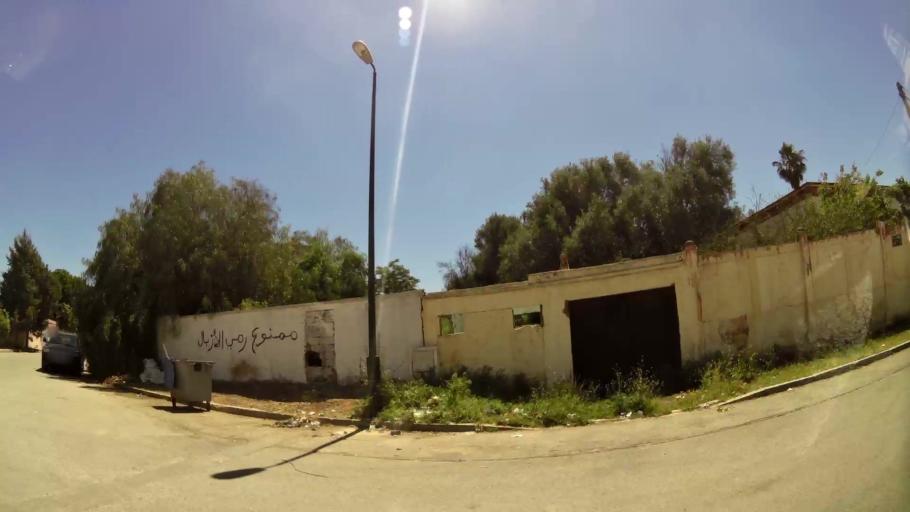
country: MA
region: Meknes-Tafilalet
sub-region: Meknes
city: Meknes
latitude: 33.8888
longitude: -5.5455
